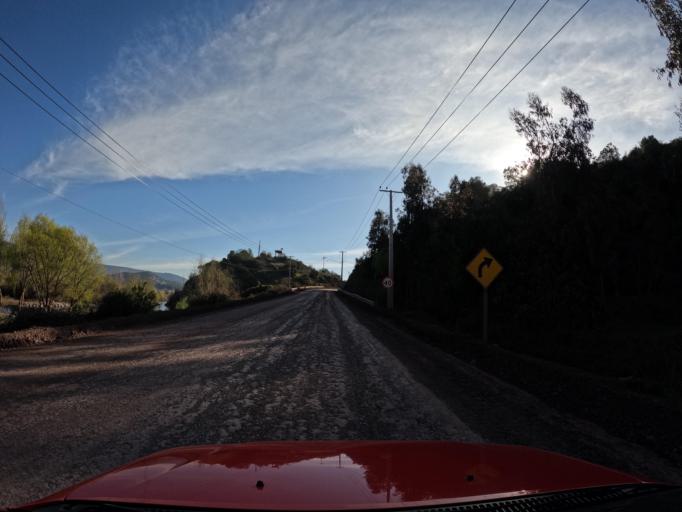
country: CL
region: Maule
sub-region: Provincia de Curico
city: Teno
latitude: -34.9691
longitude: -70.9464
